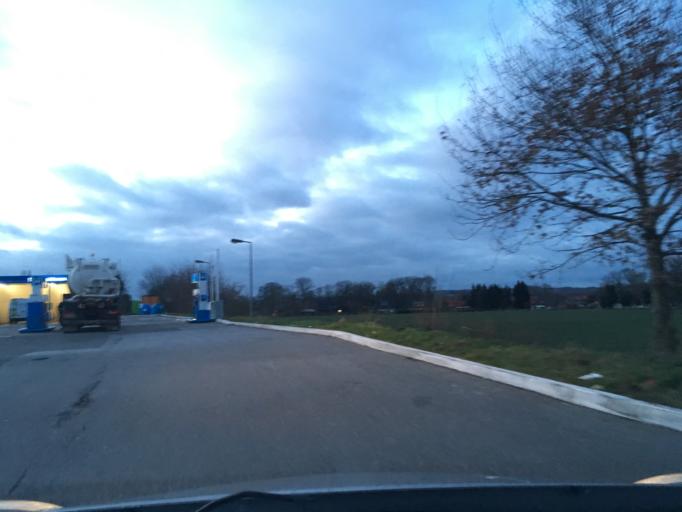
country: DE
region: Lower Saxony
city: Stelle
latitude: 53.3908
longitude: 10.0459
